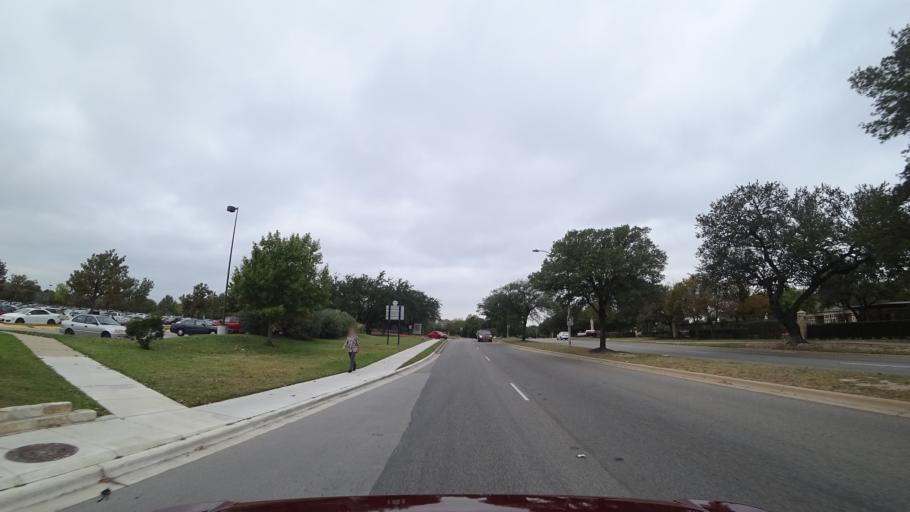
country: US
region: Texas
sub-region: Williamson County
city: Cedar Park
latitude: 30.4821
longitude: -97.8343
